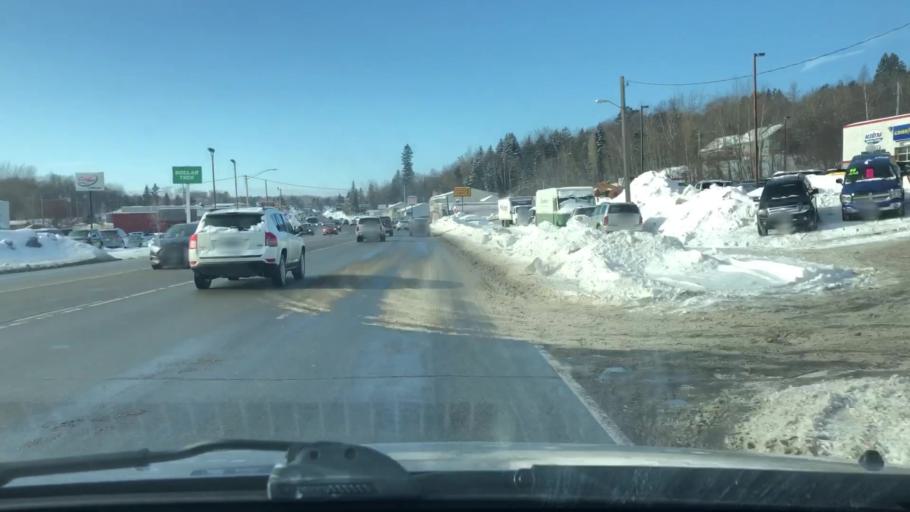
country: US
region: Minnesota
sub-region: Saint Louis County
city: Duluth
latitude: 46.8003
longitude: -92.1226
